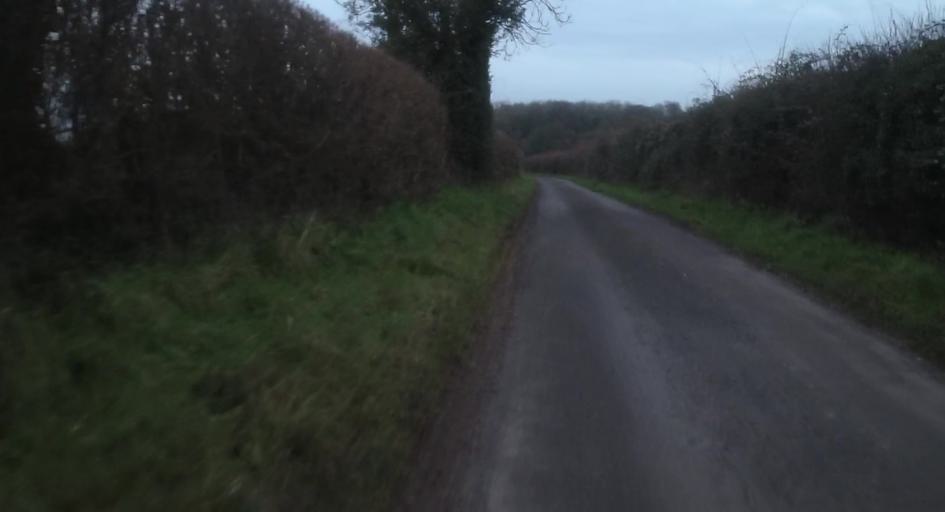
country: GB
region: England
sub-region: Hampshire
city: Overton
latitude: 51.2509
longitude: -1.3061
